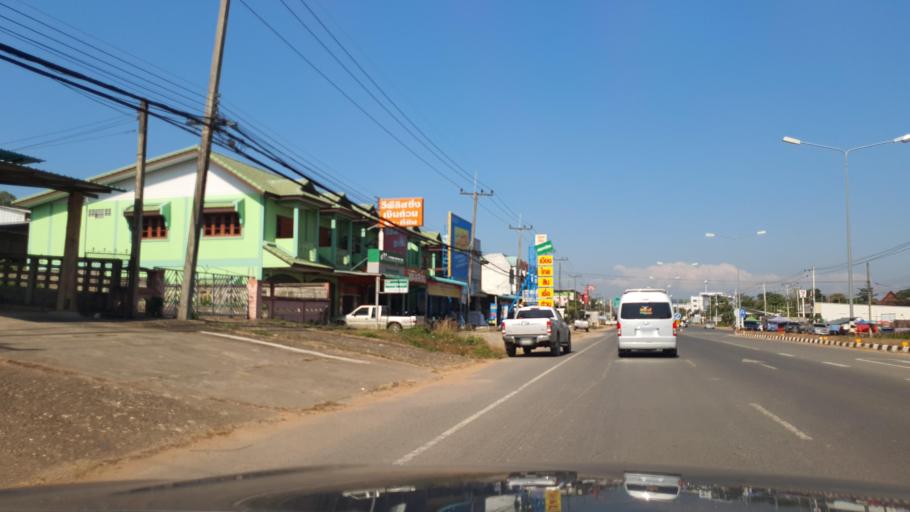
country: TH
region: Nan
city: Pua
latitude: 19.1680
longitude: 100.9230
